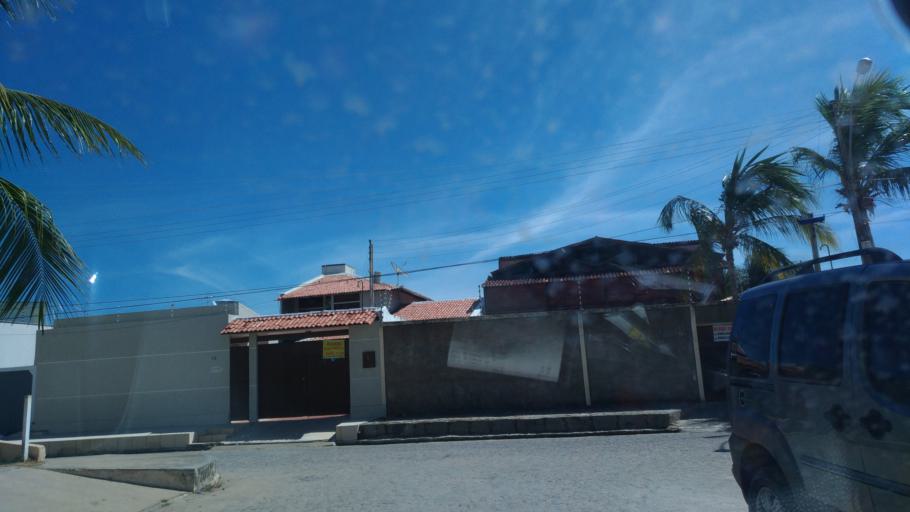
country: BR
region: Alagoas
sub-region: Marechal Deodoro
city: Marechal Deodoro
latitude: -9.7676
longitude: -35.8458
